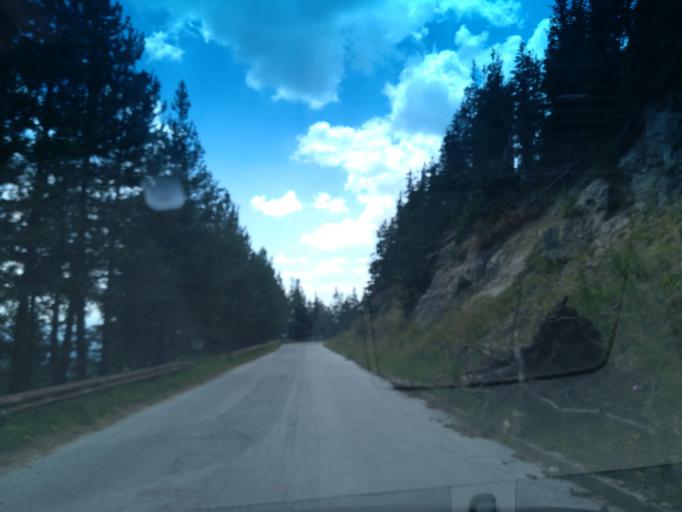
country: BG
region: Smolyan
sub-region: Obshtina Chepelare
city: Chepelare
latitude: 41.6850
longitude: 24.7527
